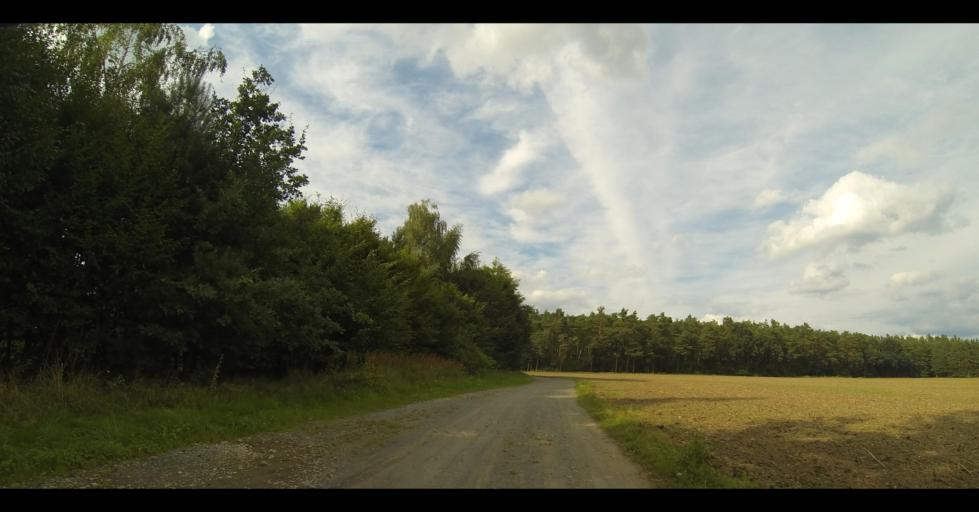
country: DE
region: Saxony
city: Radeburg
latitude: 51.2146
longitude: 13.7485
